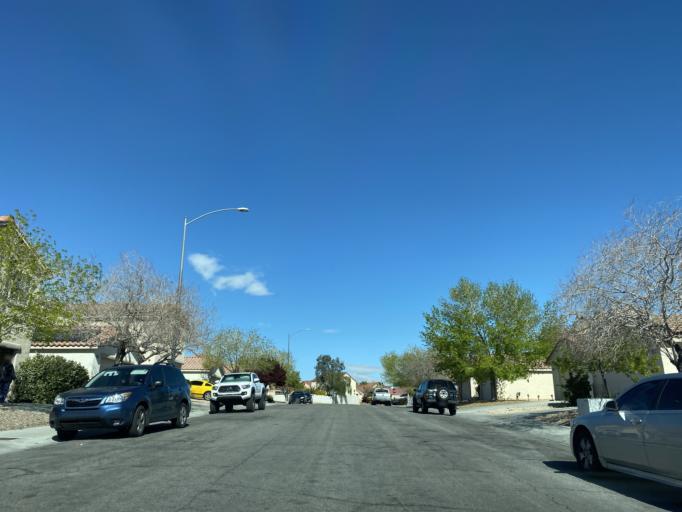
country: US
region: Nevada
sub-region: Clark County
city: Summerlin South
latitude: 36.3041
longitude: -115.2871
